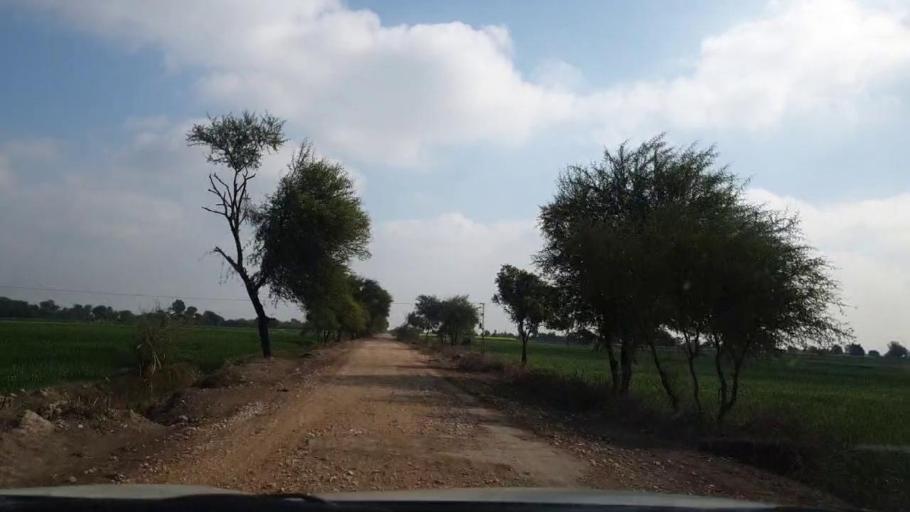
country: PK
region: Sindh
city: Berani
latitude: 25.7774
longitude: 68.9734
